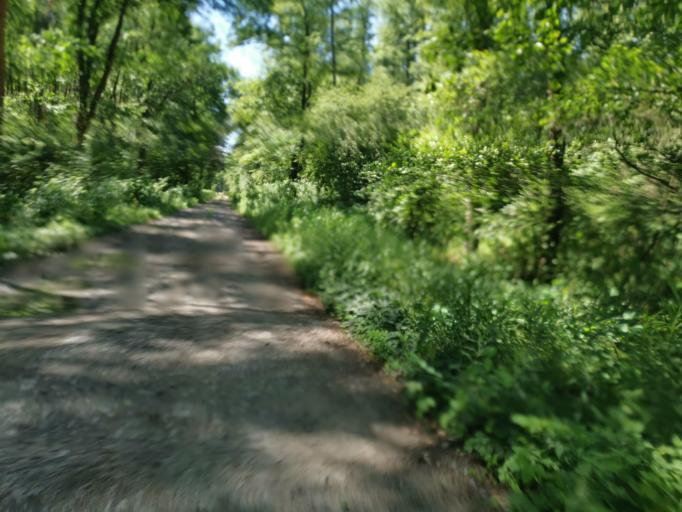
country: CZ
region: South Moravian
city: Bzenec
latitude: 48.9644
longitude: 17.2656
